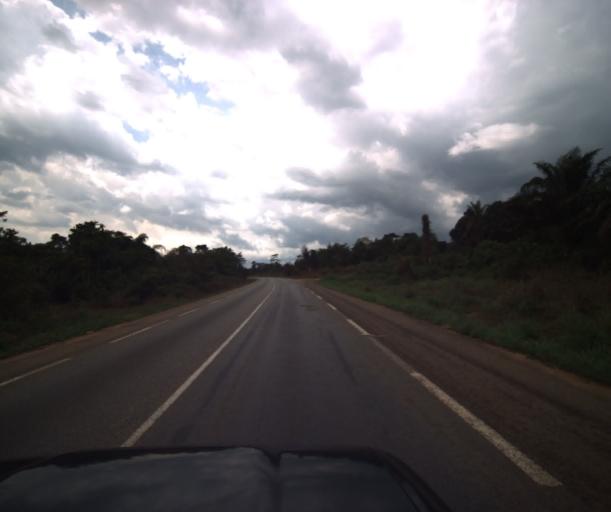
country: CM
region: Littoral
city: Edea
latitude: 3.8533
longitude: 10.0851
